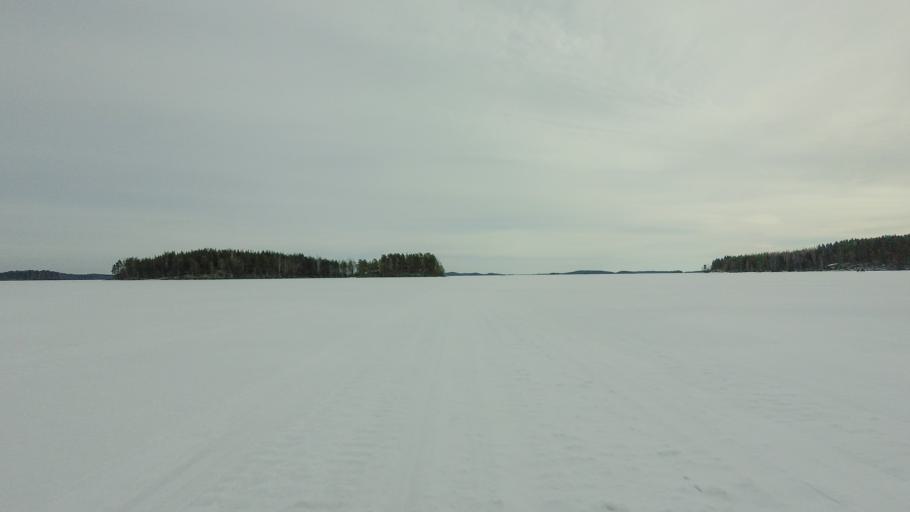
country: FI
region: Southern Savonia
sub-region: Savonlinna
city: Rantasalmi
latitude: 62.1138
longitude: 28.3701
